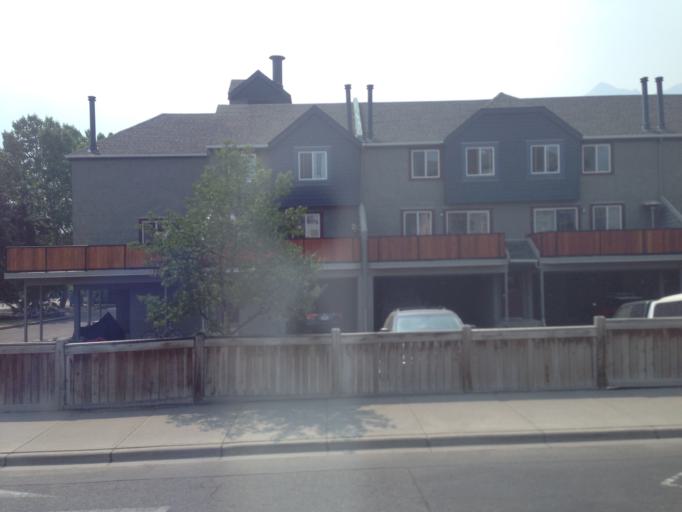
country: CA
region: Alberta
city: Canmore
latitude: 51.0914
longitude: -115.3565
